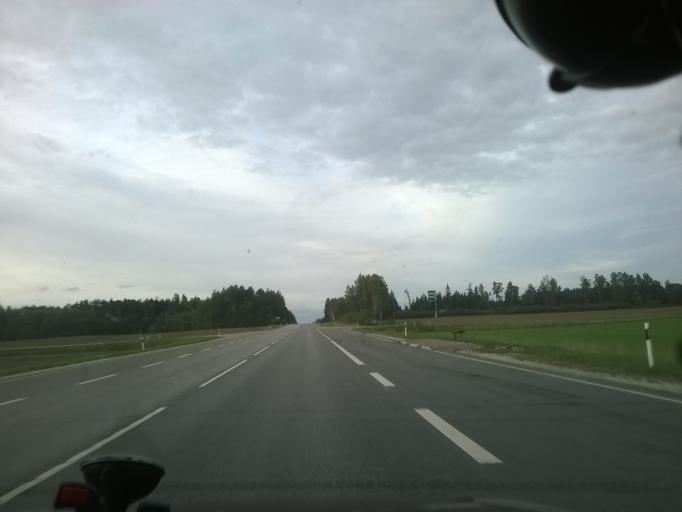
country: EE
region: Vorumaa
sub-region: Voru linn
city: Voru
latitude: 57.9331
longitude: 26.7984
